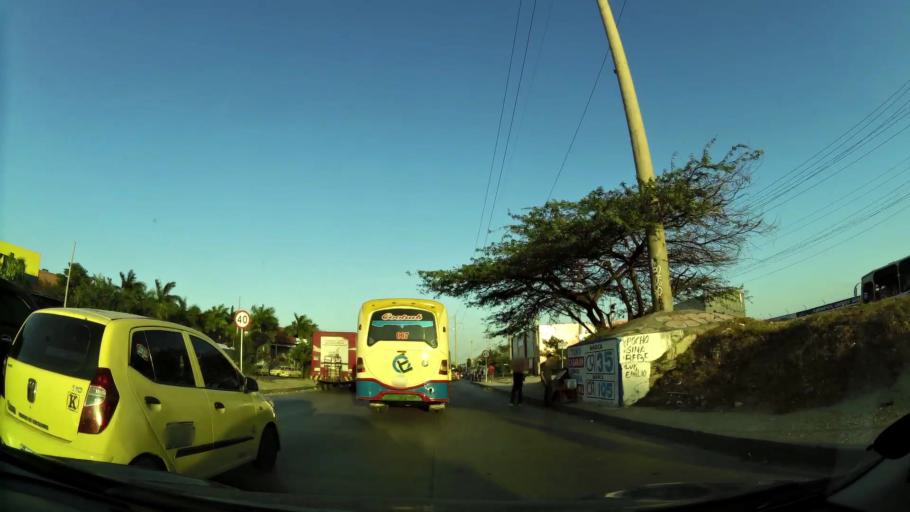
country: CO
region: Atlantico
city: Soledad
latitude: 10.9235
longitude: -74.7977
